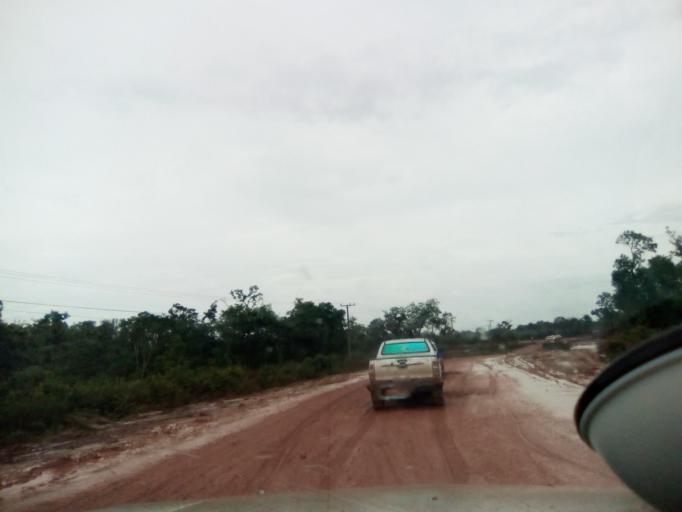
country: LA
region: Attapu
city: Attapu
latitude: 14.6929
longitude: 106.5361
